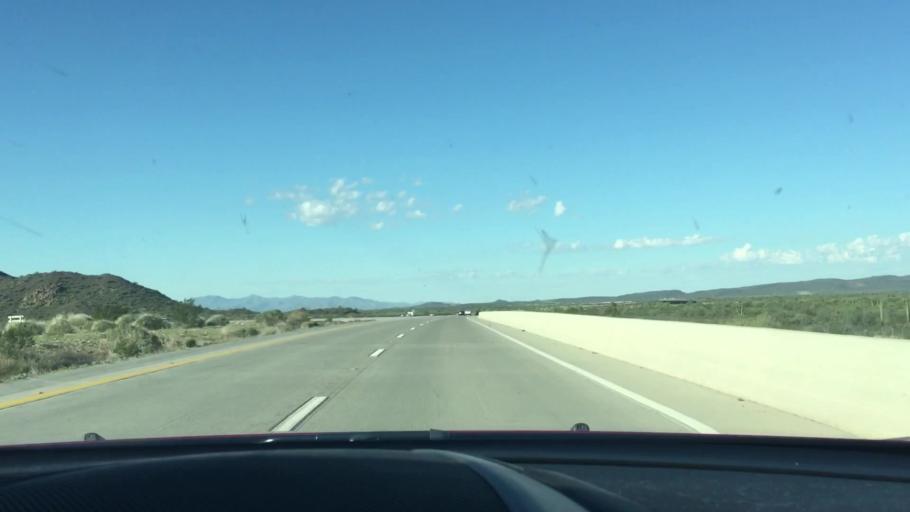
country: US
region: Arizona
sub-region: Maricopa County
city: Anthem
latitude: 33.7811
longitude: -112.2075
